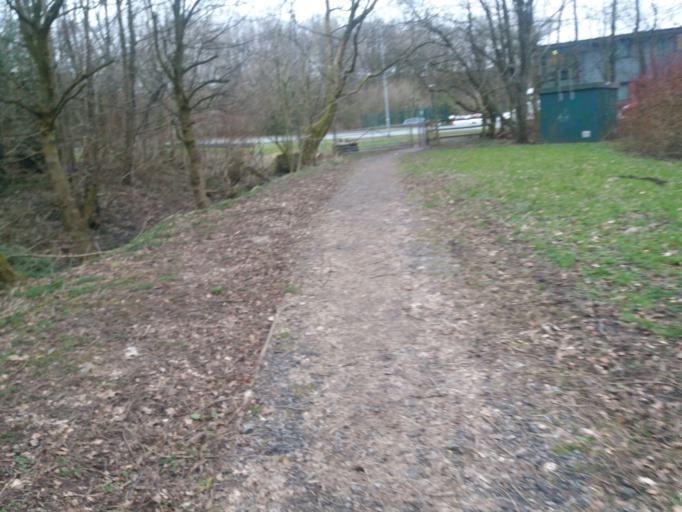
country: GB
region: England
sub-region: Lancashire
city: Chorley
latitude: 53.6686
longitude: -2.6264
